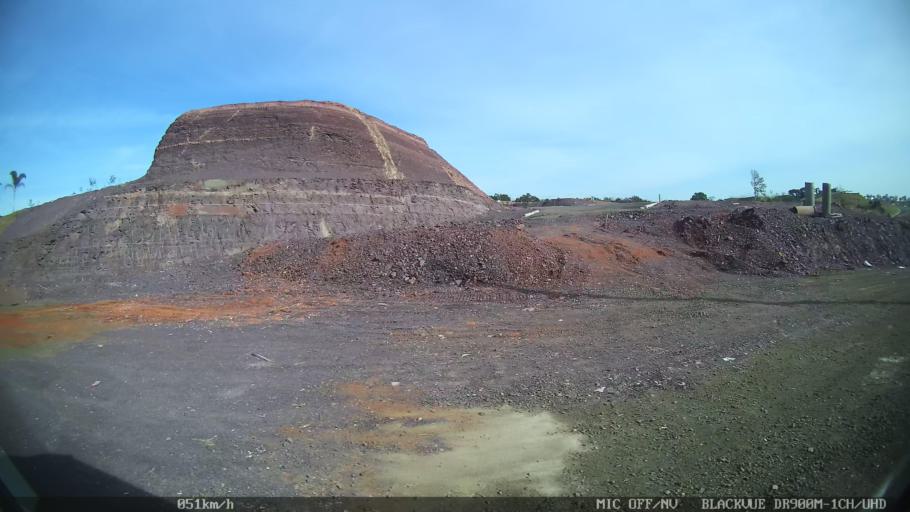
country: BR
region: Sao Paulo
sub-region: Piracicaba
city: Piracicaba
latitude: -22.7097
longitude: -47.6772
